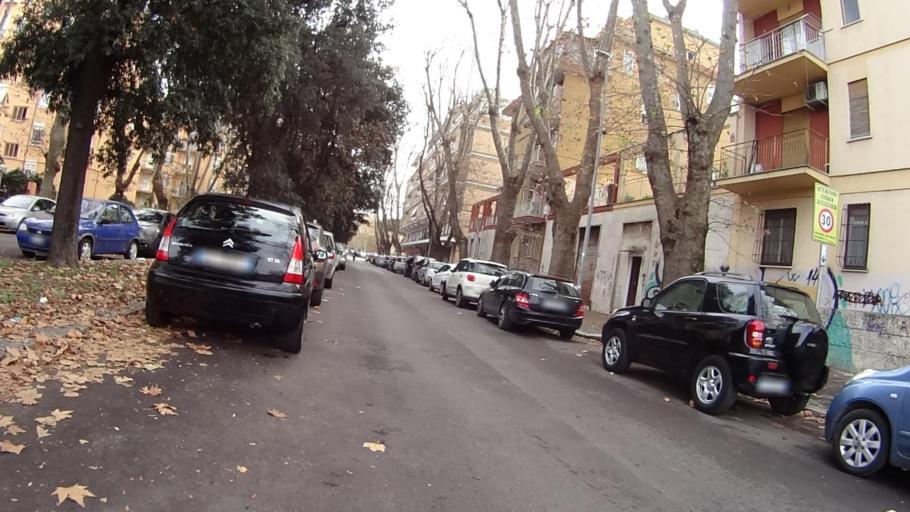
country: IT
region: Latium
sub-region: Citta metropolitana di Roma Capitale
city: Lido di Ostia
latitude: 41.7332
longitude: 12.2816
